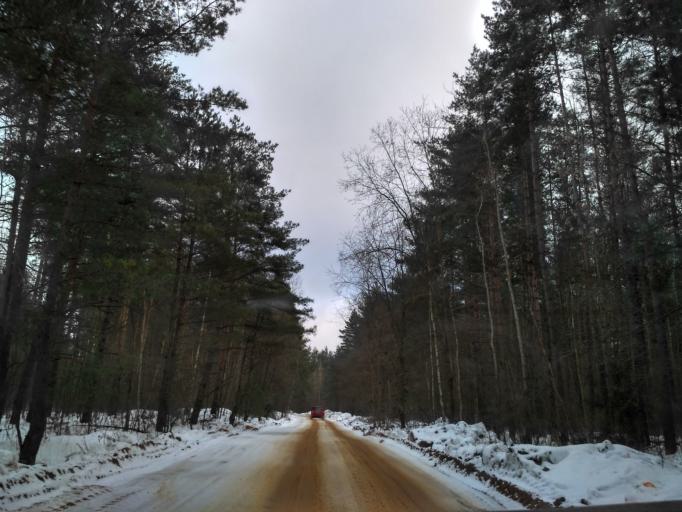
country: BY
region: Minsk
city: Vyaliki Trastsyanets
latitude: 53.9212
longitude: 27.7020
